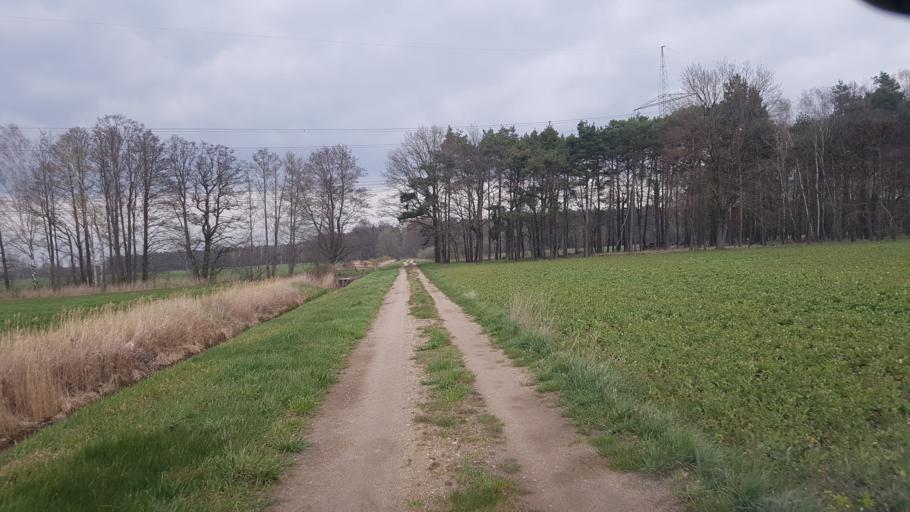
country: DE
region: Brandenburg
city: Sallgast
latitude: 51.6289
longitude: 13.8768
